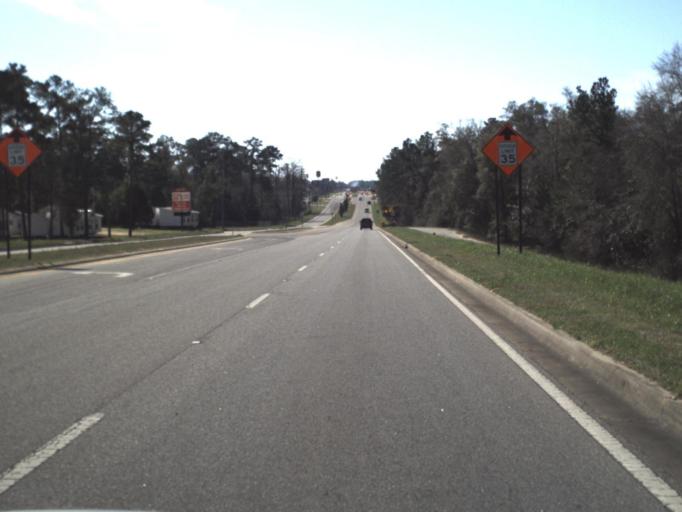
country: US
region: Florida
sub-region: Jackson County
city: Marianna
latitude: 30.7346
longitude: -85.1855
